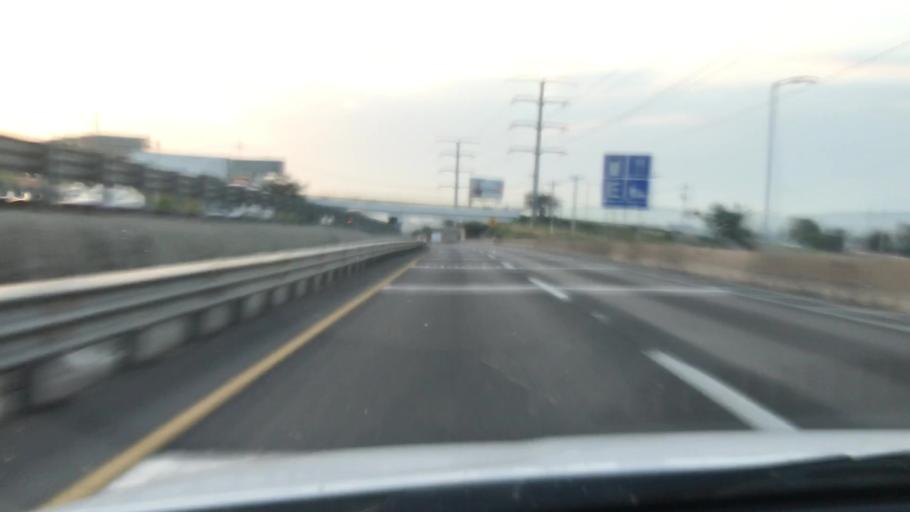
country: MX
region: Jalisco
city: Tonala
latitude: 20.6153
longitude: -103.2427
